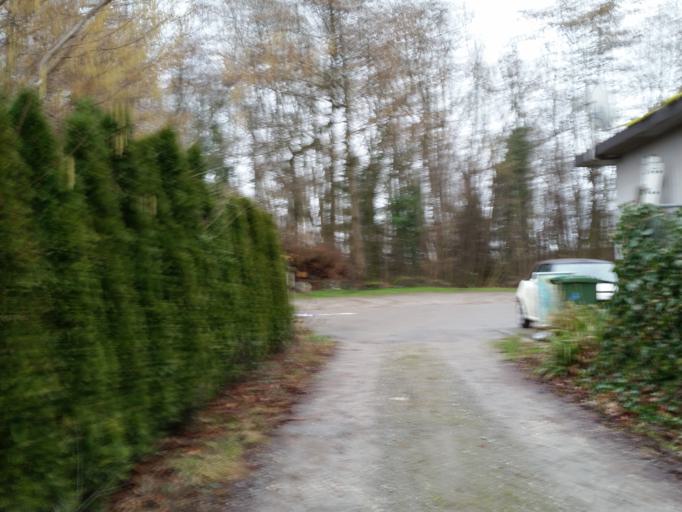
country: CH
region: Thurgau
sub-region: Arbon District
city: Egnach
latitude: 47.5482
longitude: 9.3843
